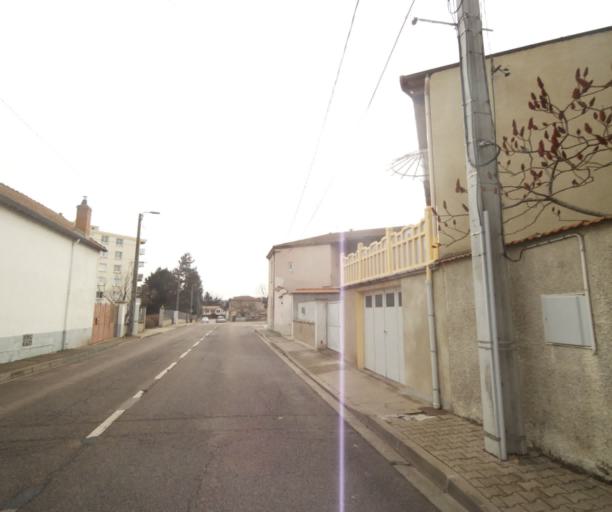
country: FR
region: Rhone-Alpes
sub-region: Departement de la Loire
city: Roanne
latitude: 46.0254
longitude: 4.0685
